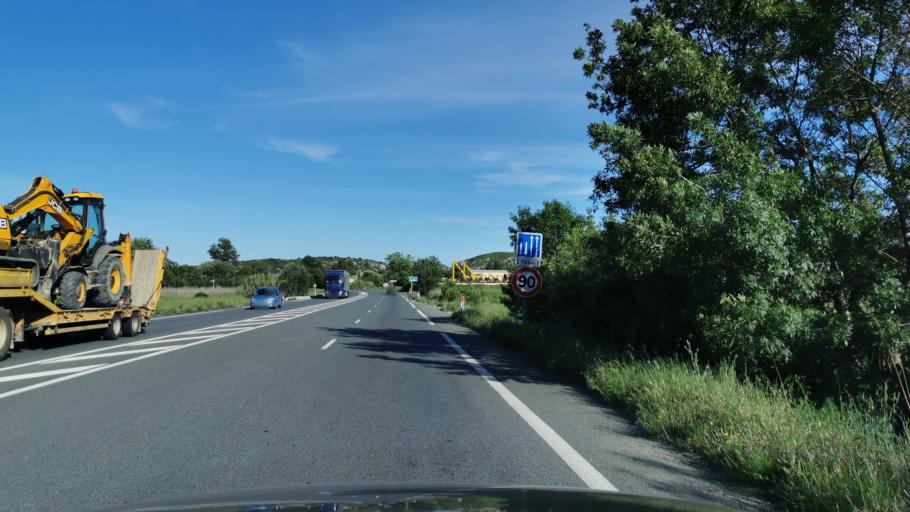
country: FR
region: Languedoc-Roussillon
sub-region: Departement de l'Aude
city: Canet
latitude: 43.2131
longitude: 2.8670
